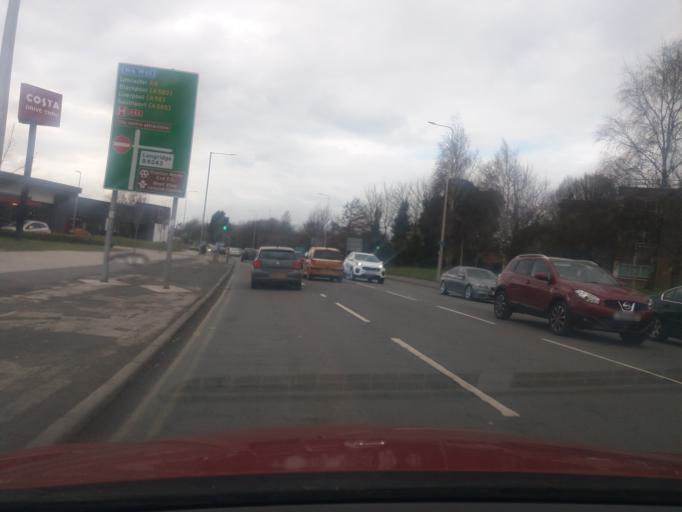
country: GB
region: England
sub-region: Lancashire
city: Preston
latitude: 53.7605
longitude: -2.6877
